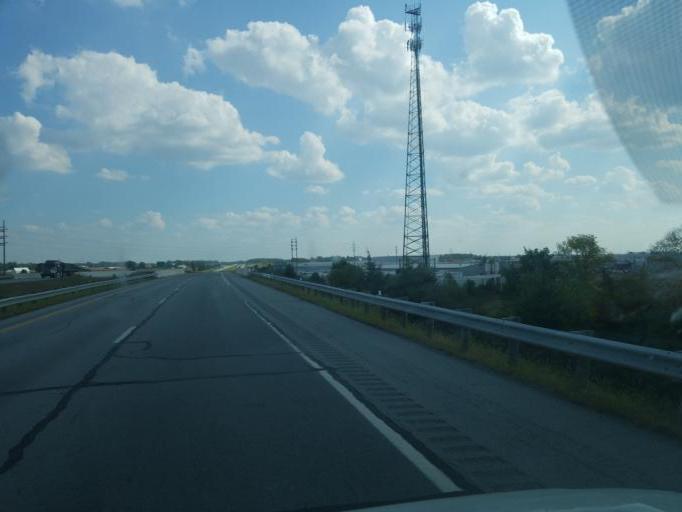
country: US
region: Ohio
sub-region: Allen County
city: Delphos
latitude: 40.8601
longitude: -84.3223
